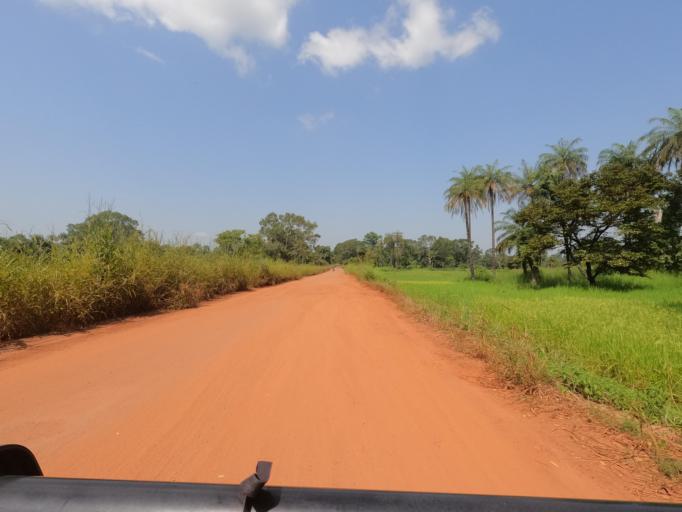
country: GW
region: Oio
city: Bissora
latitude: 12.3574
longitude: -15.7691
